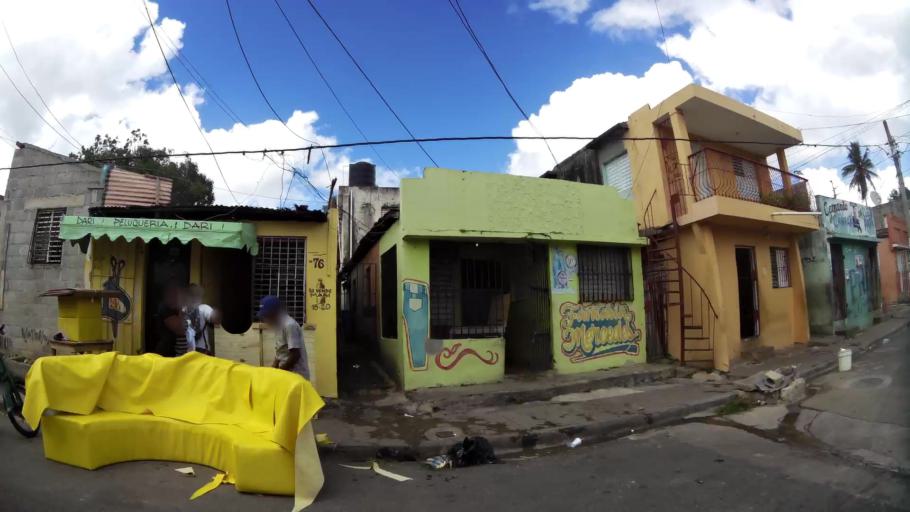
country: DO
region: Nacional
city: Ensanche Luperon
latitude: 18.4938
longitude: -69.8844
